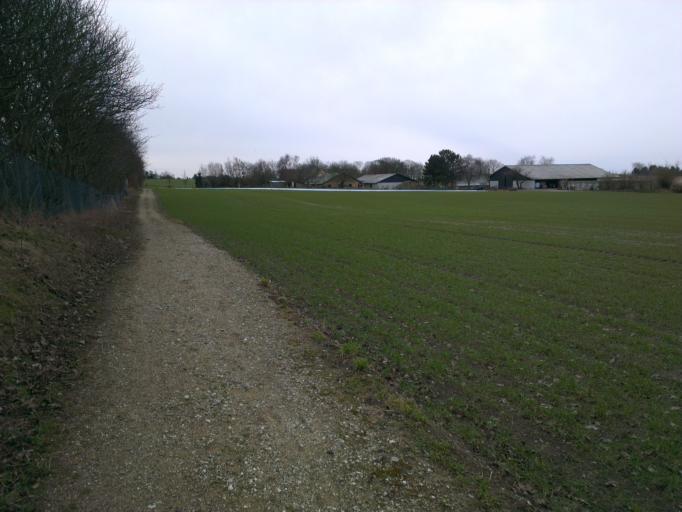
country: DK
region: Zealand
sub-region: Lejre Kommune
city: Ejby
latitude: 55.7608
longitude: 11.8742
